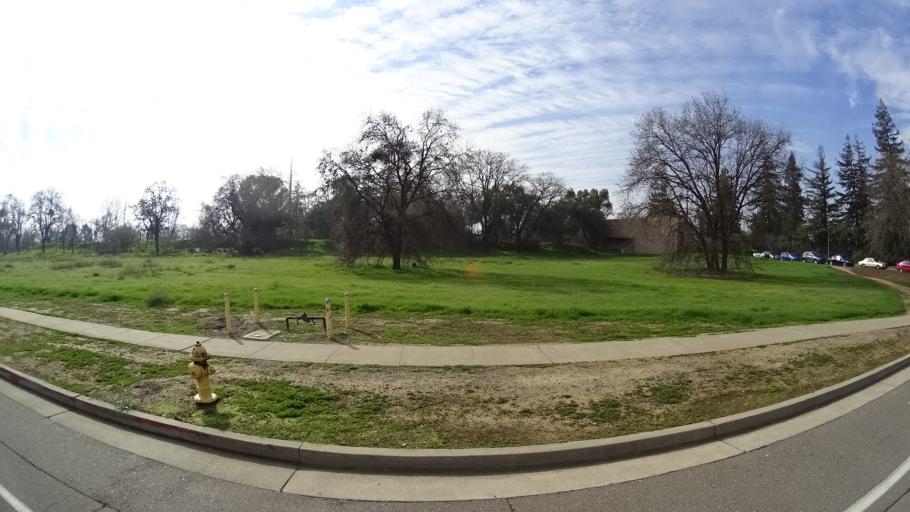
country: US
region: California
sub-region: Yolo County
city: Davis
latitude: 38.5389
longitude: -121.7356
